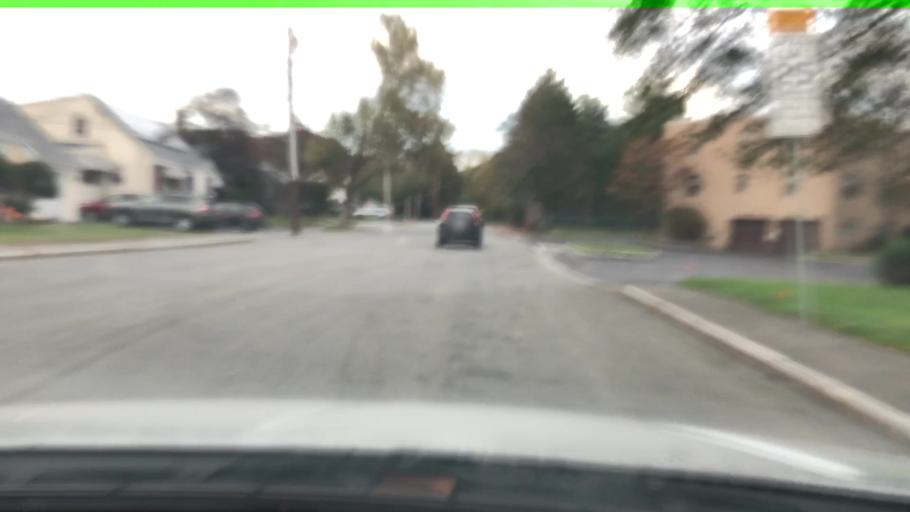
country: US
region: Massachusetts
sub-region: Middlesex County
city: Belmont
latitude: 42.4161
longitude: -71.1933
